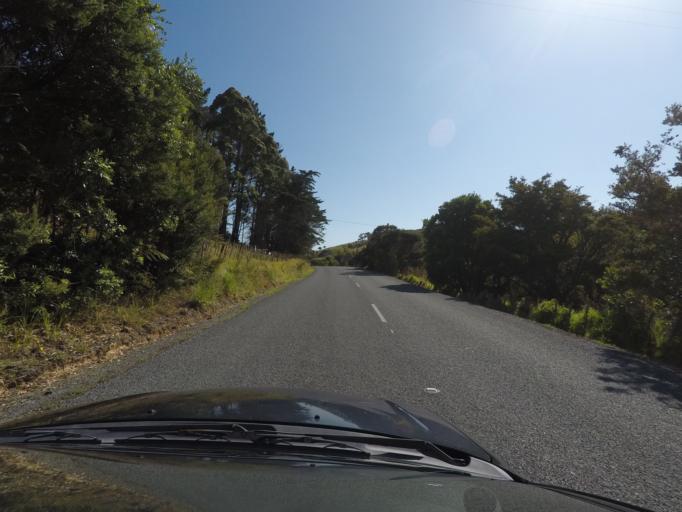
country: NZ
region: Auckland
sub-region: Auckland
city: Warkworth
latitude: -36.2768
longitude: 174.7917
